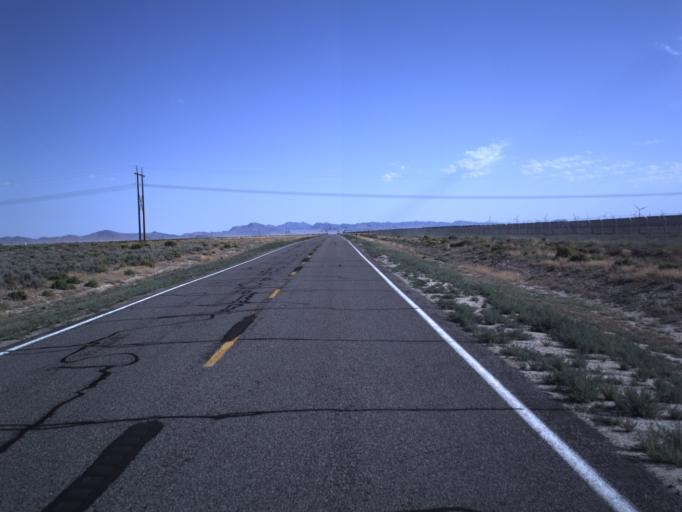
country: US
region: Utah
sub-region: Beaver County
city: Milford
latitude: 38.4850
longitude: -112.9911
